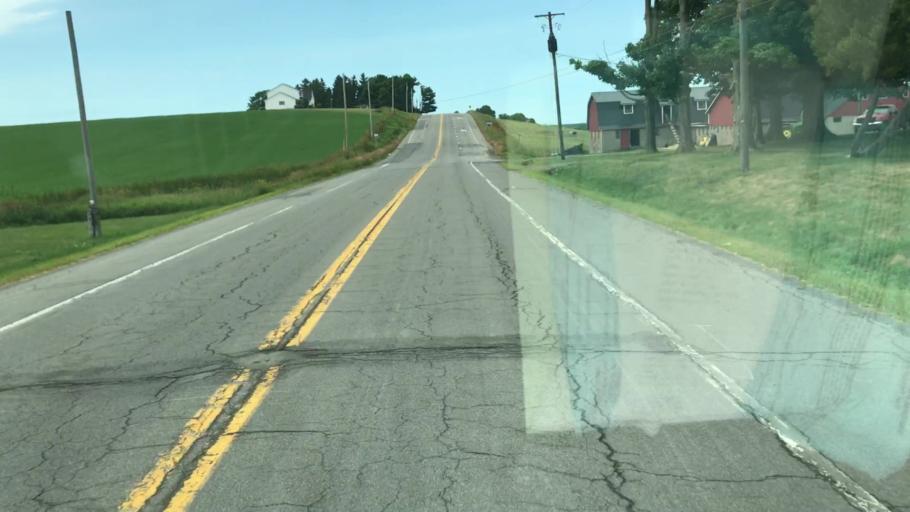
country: US
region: New York
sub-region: Onondaga County
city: Marcellus
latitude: 42.9347
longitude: -76.3615
